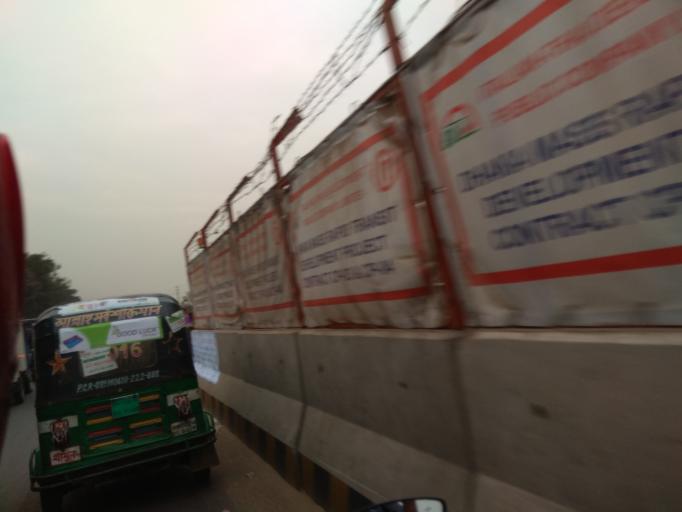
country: BD
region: Dhaka
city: Azimpur
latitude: 23.7766
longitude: 90.3807
